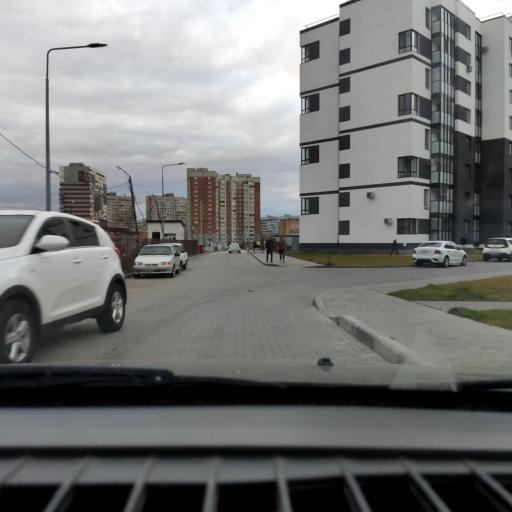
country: RU
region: Samara
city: Tol'yatti
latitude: 53.5255
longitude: 49.3393
